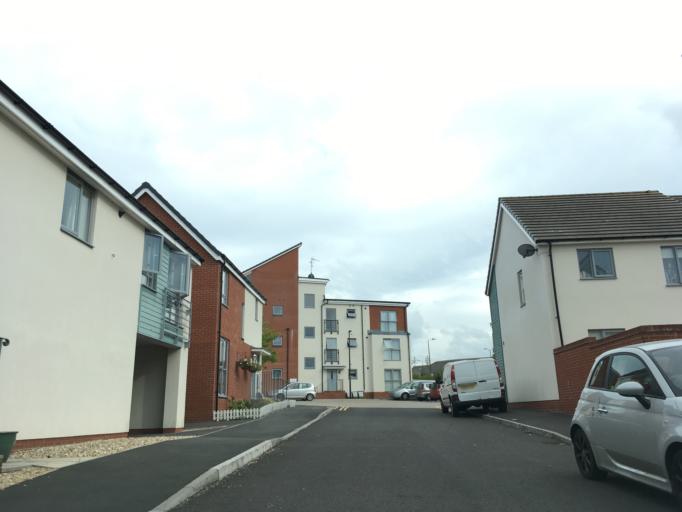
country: GB
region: England
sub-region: South Gloucestershire
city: Stoke Gifford
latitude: 51.4983
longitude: -2.5591
